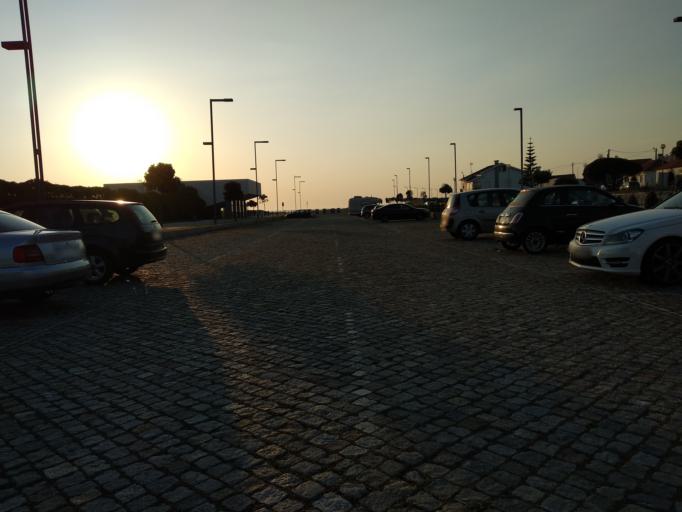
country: PT
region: Viana do Castelo
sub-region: Caminha
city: Vila Praia de Ancora
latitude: 41.8168
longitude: -8.8689
